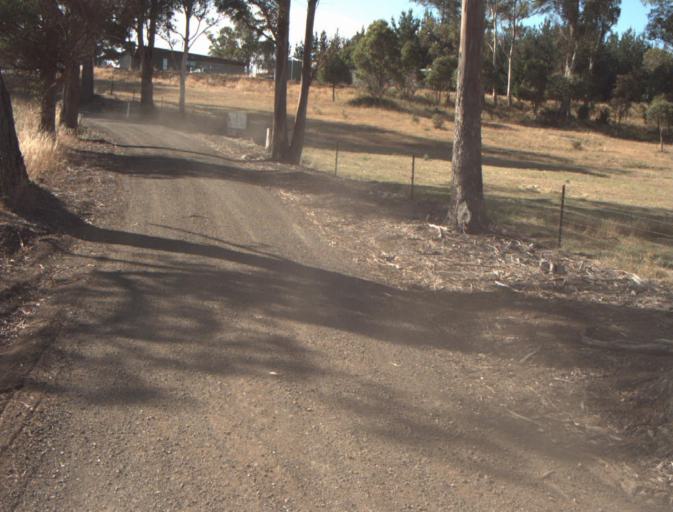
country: AU
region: Tasmania
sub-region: Dorset
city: Bridport
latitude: -41.1441
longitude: 147.2122
